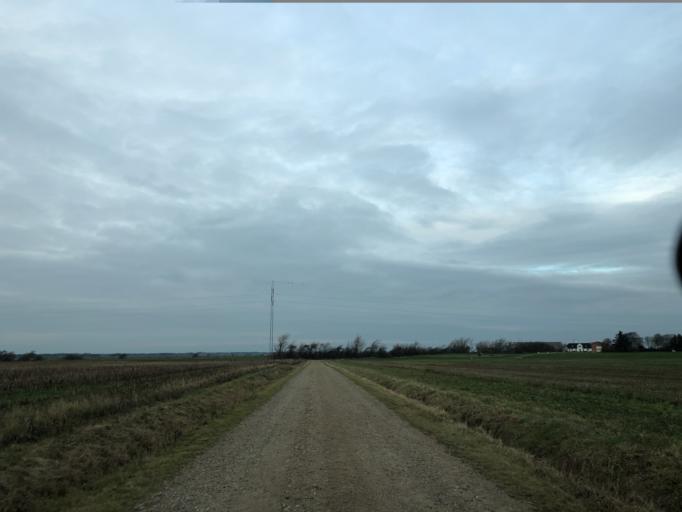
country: DK
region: Central Jutland
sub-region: Holstebro Kommune
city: Ulfborg
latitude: 56.2739
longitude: 8.2171
